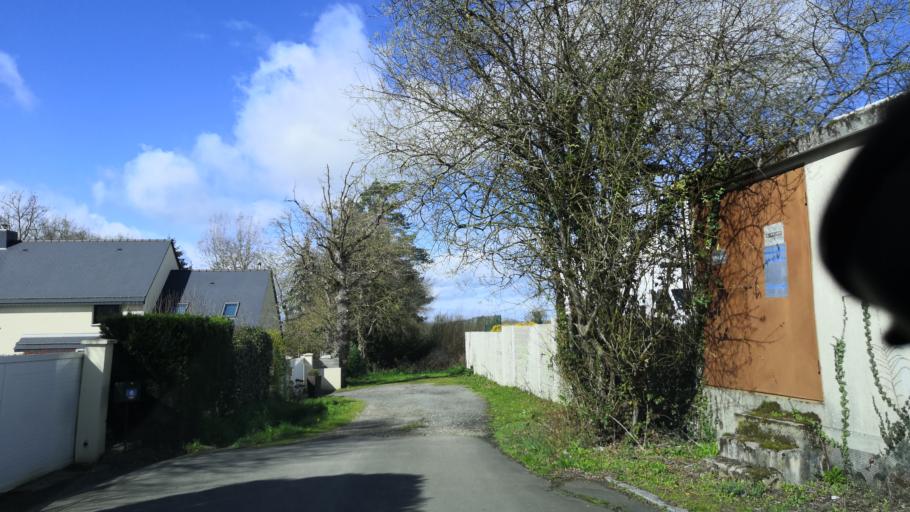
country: FR
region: Brittany
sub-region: Departement d'Ille-et-Vilaine
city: Bedee
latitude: 48.1838
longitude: -1.9466
